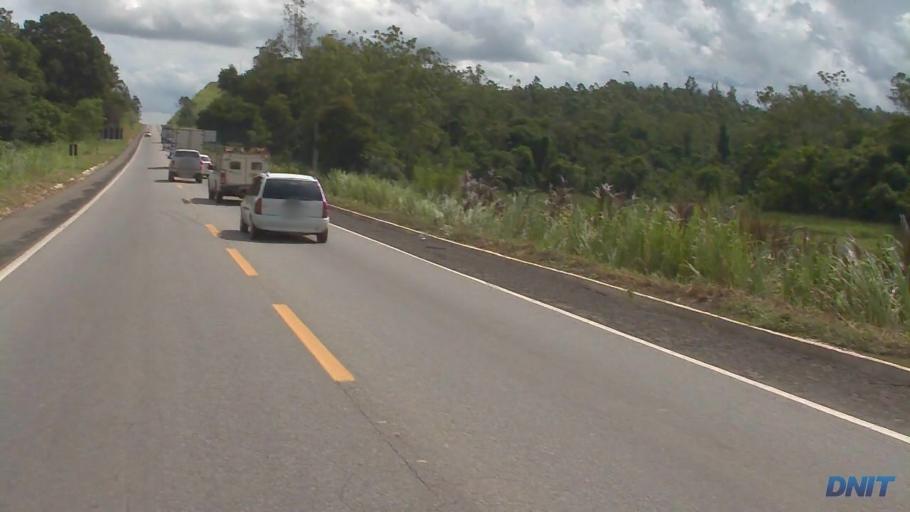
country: BR
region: Minas Gerais
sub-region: Ipatinga
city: Ipatinga
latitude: -19.4307
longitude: -42.5047
